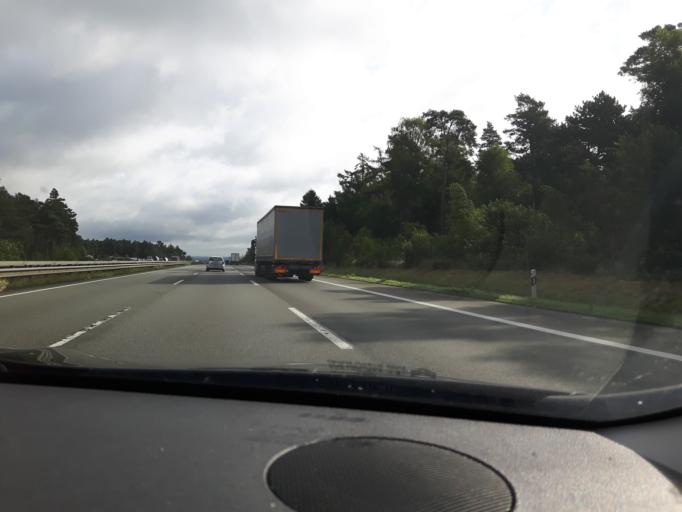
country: DE
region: Lower Saxony
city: Heidenau
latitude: 53.3466
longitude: 9.6677
